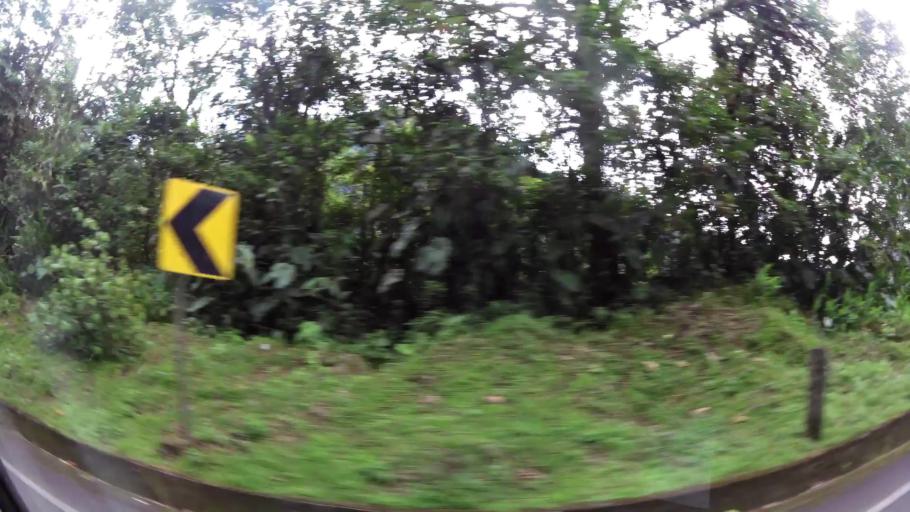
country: EC
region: Pastaza
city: Puyo
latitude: -1.4250
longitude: -78.1761
